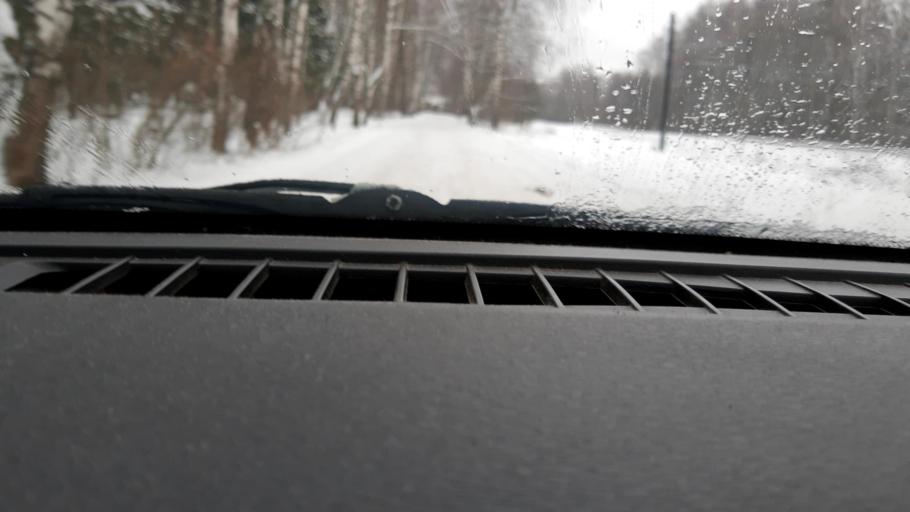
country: RU
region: Nizjnij Novgorod
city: Afonino
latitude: 56.1876
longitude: 44.0756
